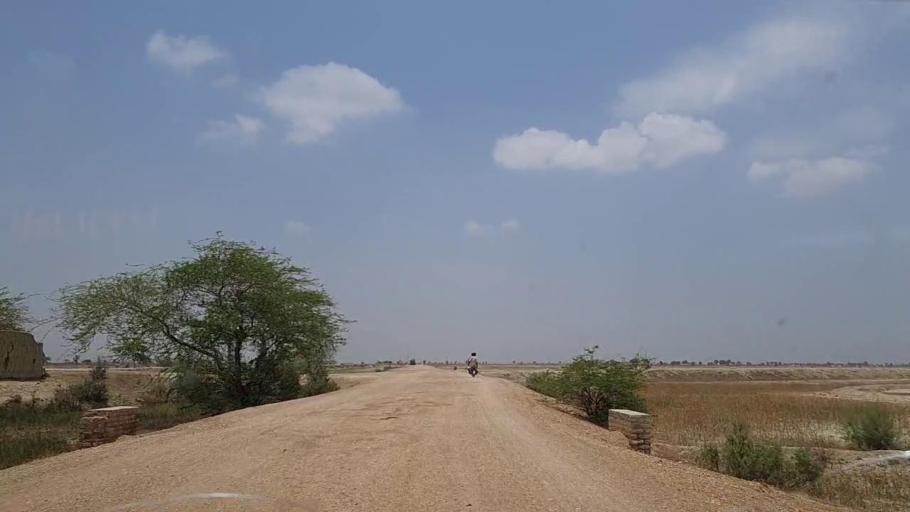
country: PK
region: Sindh
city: Johi
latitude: 26.7652
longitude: 67.6610
